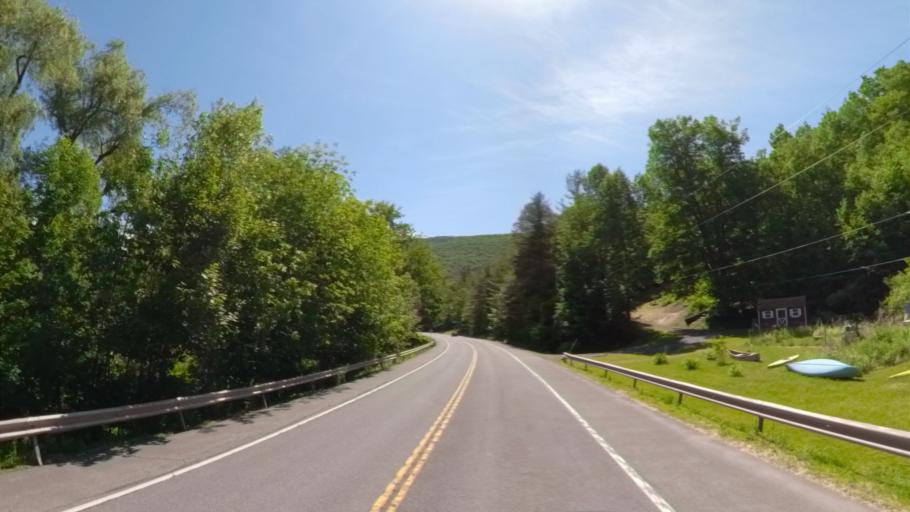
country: US
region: New York
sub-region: Ulster County
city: Shokan
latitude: 42.1022
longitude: -74.4417
